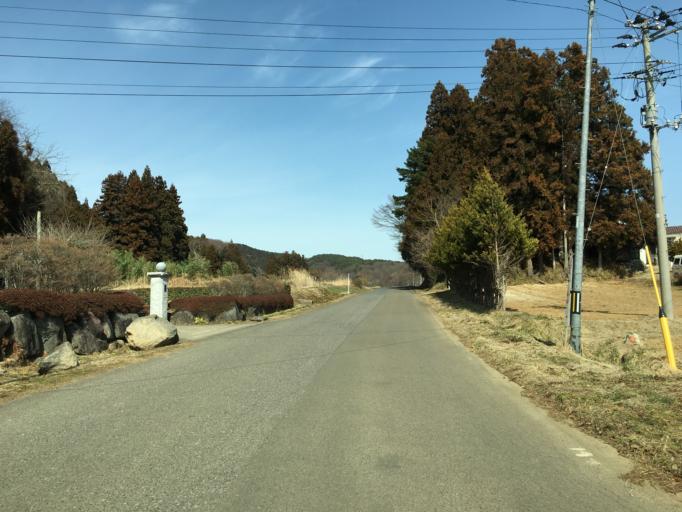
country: JP
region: Fukushima
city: Nihommatsu
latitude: 37.5928
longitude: 140.3854
